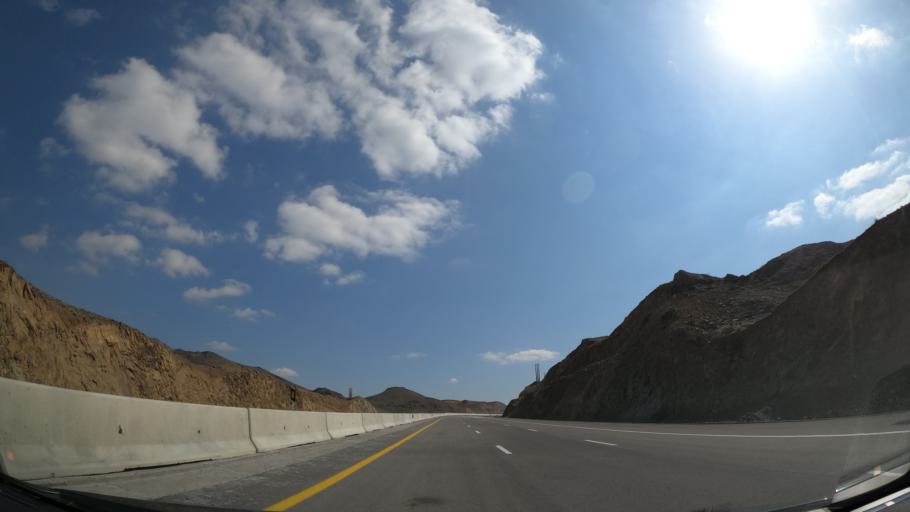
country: IR
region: Alborz
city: Nazarabad
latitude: 35.6845
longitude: 50.6393
